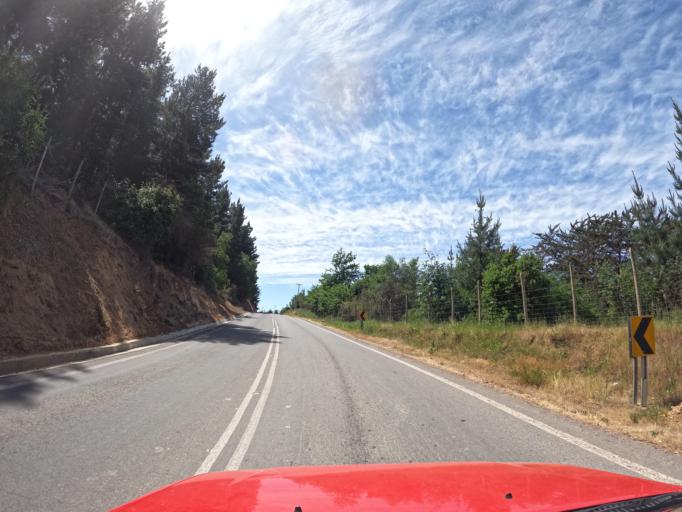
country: CL
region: Maule
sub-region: Provincia de Talca
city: Talca
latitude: -34.9950
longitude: -71.8090
